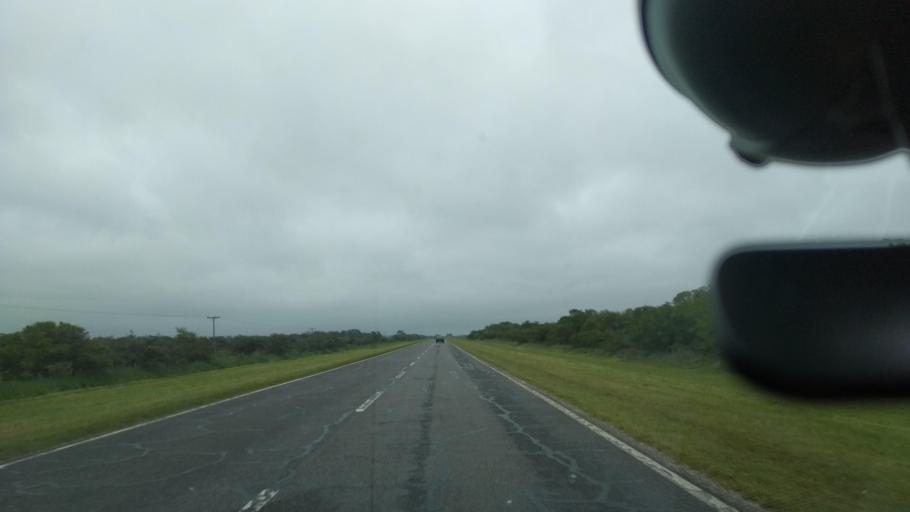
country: AR
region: Buenos Aires
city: Veronica
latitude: -35.6464
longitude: -57.3167
